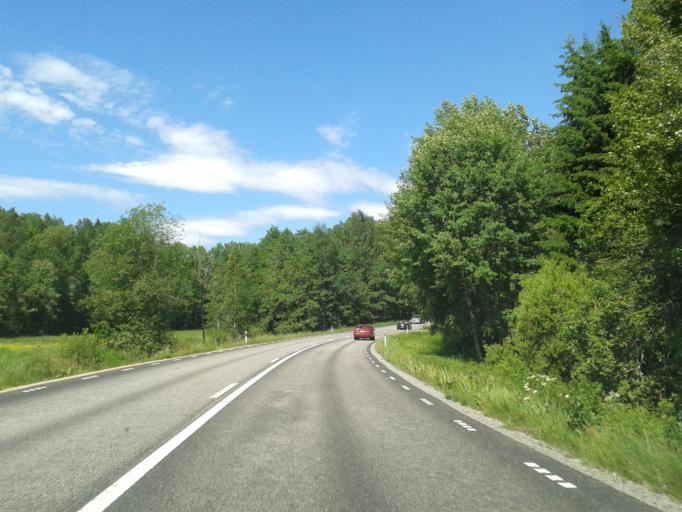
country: SE
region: Vaestra Goetaland
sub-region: Orust
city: Henan
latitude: 58.3191
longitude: 11.6806
